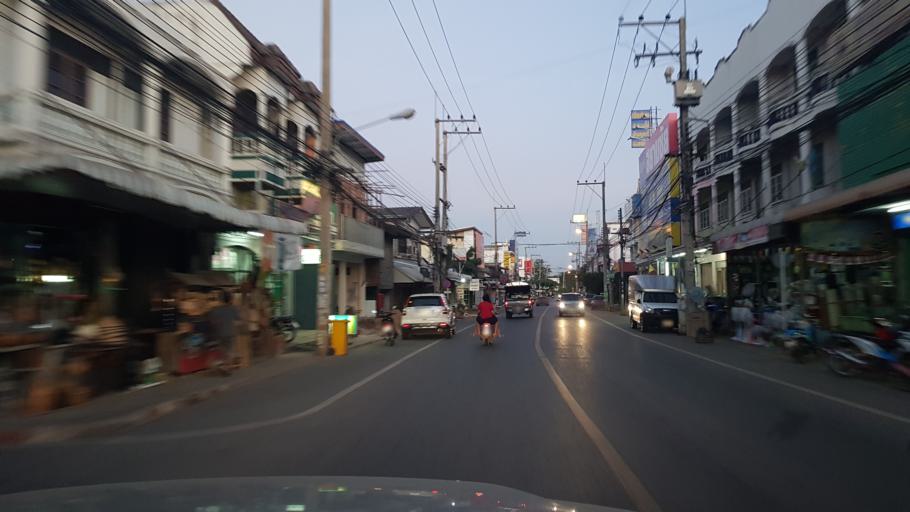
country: TH
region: Chaiyaphum
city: Phu Khiao
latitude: 16.3660
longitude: 102.1364
